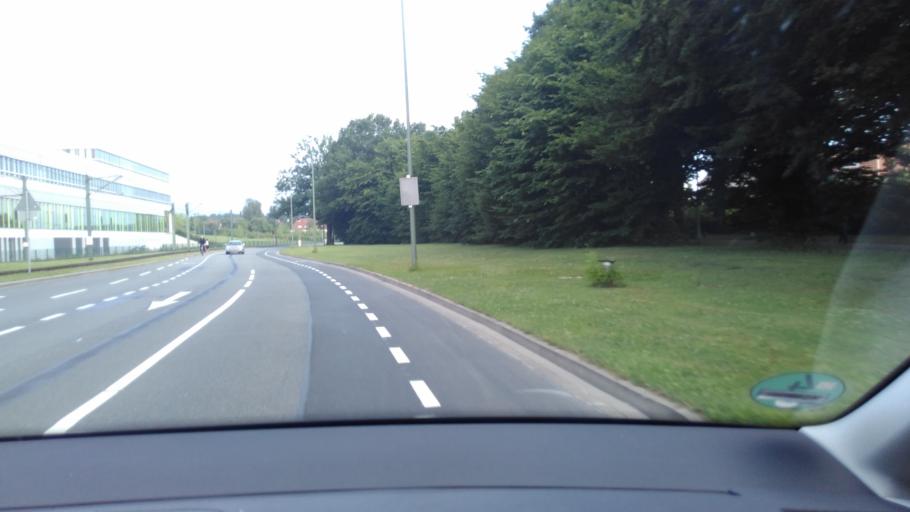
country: DE
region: North Rhine-Westphalia
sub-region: Regierungsbezirk Detmold
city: Bielefeld
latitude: 52.0402
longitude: 8.4949
